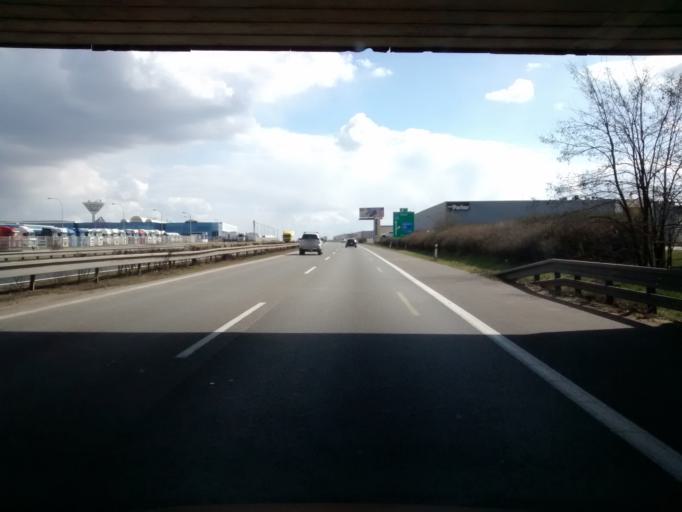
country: CZ
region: Central Bohemia
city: Zdiby
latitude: 50.1846
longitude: 14.4461
